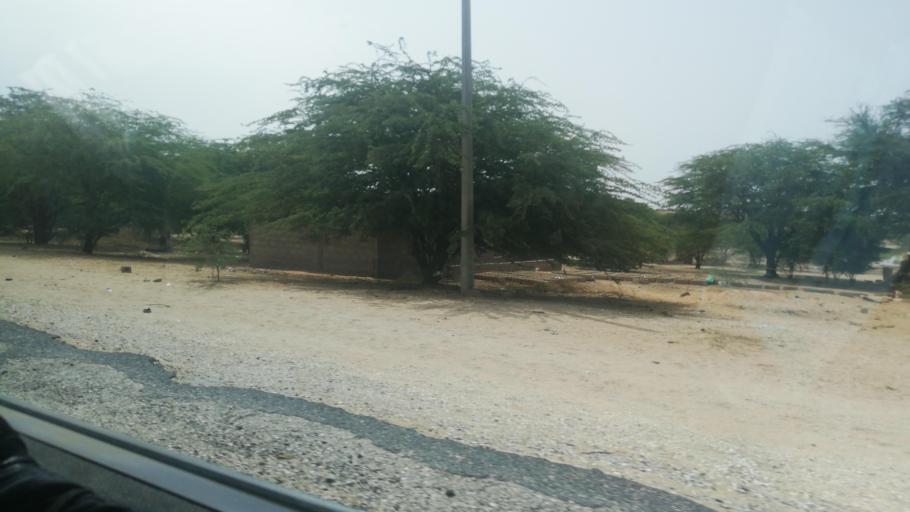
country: SN
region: Saint-Louis
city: Saint-Louis
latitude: 16.0798
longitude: -16.3676
